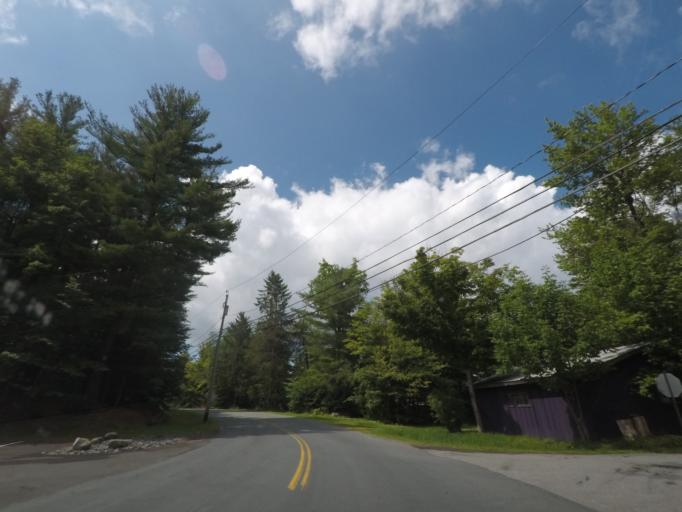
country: US
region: New York
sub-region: Rensselaer County
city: Averill Park
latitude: 42.6461
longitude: -73.4859
